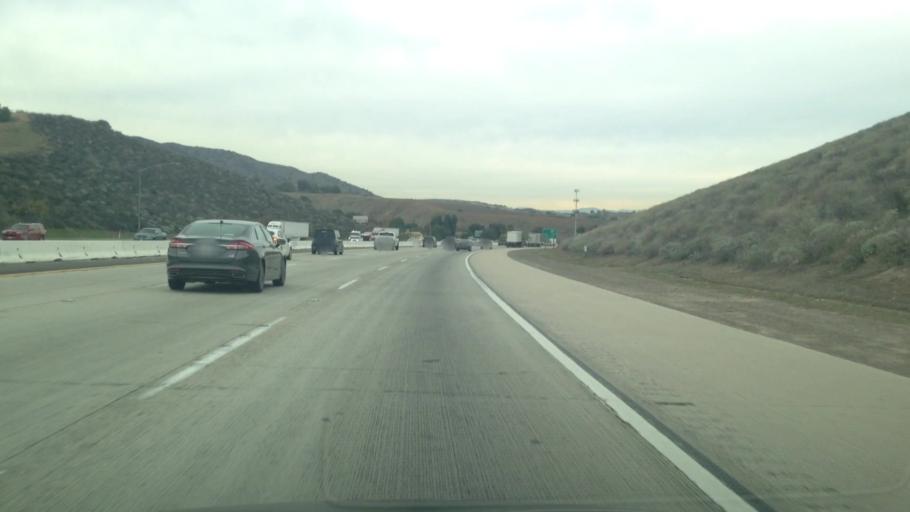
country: US
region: California
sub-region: Riverside County
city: El Cerrito
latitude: 33.7698
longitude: -117.4814
